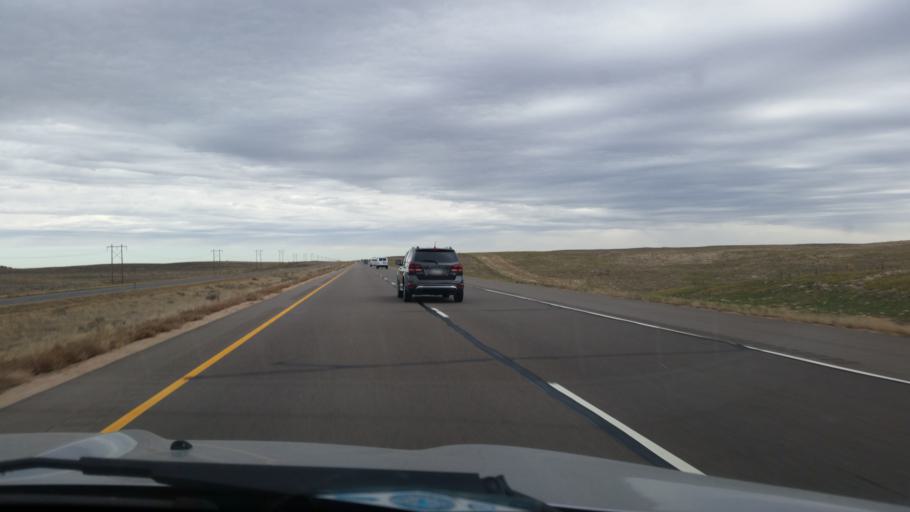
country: US
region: Colorado
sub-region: Morgan County
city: Brush
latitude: 40.3379
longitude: -103.4645
